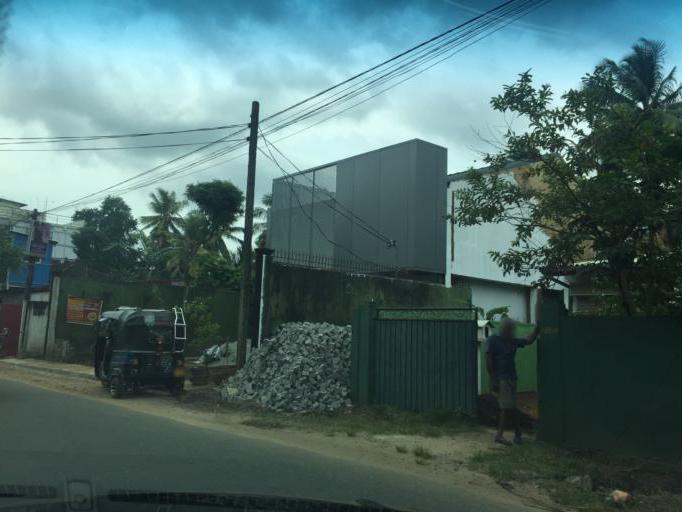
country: LK
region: Western
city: Horana South
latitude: 6.7057
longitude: 80.0693
